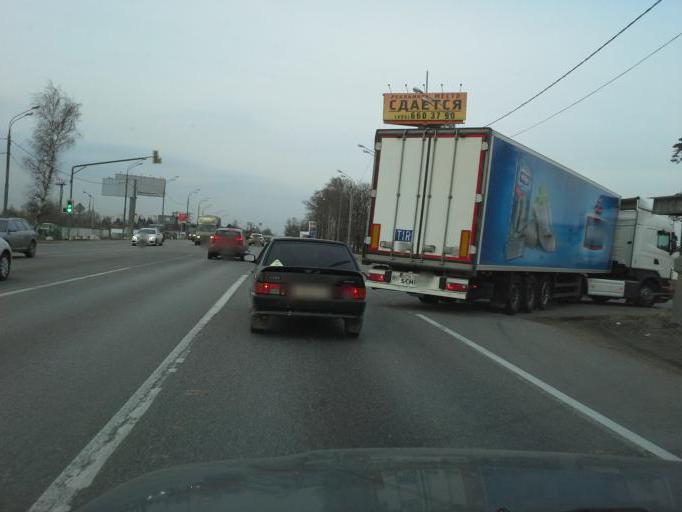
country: RU
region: Moskovskaya
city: Odintsovo
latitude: 55.6688
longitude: 37.3105
